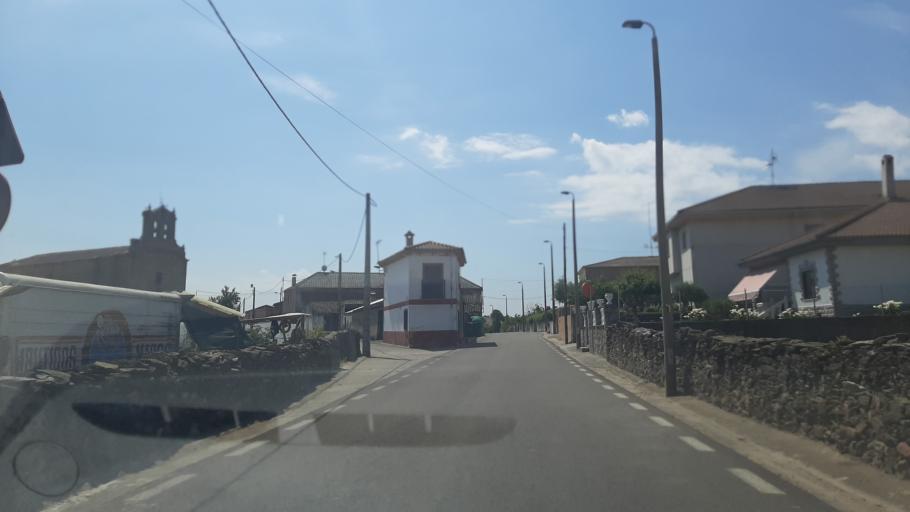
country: ES
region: Castille and Leon
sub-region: Provincia de Salamanca
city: Gallegos de Arganan
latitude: 40.6314
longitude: -6.7055
